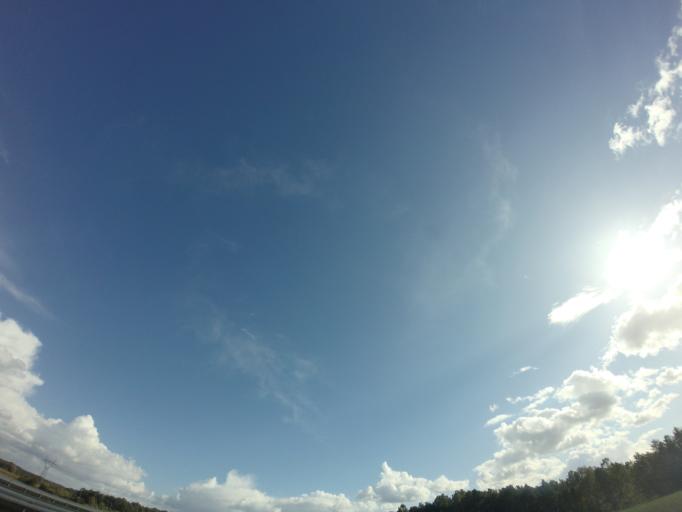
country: PL
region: Lubusz
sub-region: Powiat nowosolski
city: Nowe Miasteczko
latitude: 51.7118
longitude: 15.7474
